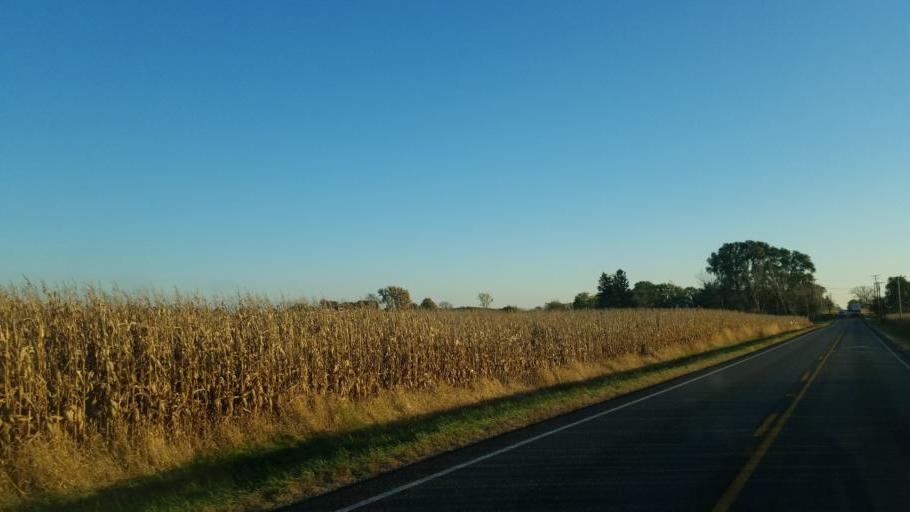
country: US
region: Ohio
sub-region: Sandusky County
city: Clyde
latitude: 41.2657
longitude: -82.9752
